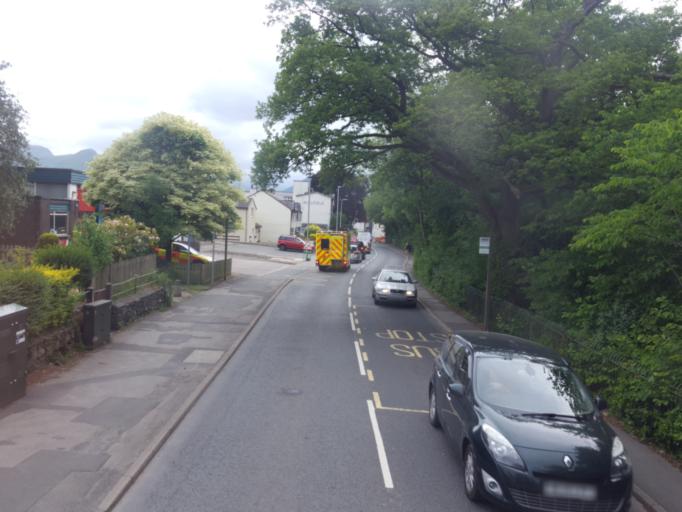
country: GB
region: England
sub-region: Cumbria
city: Keswick
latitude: 54.6029
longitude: -3.1271
